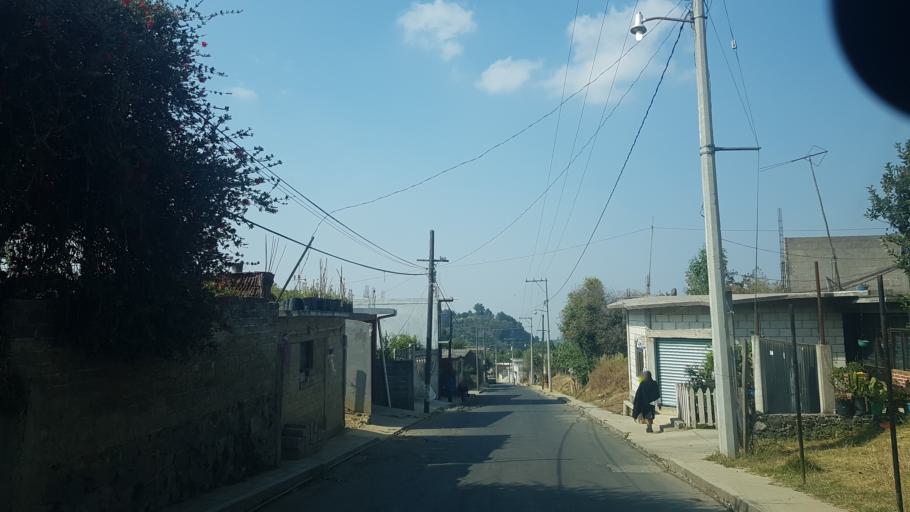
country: MX
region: Morelos
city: Hueyapan
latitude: 18.8907
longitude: -98.6798
